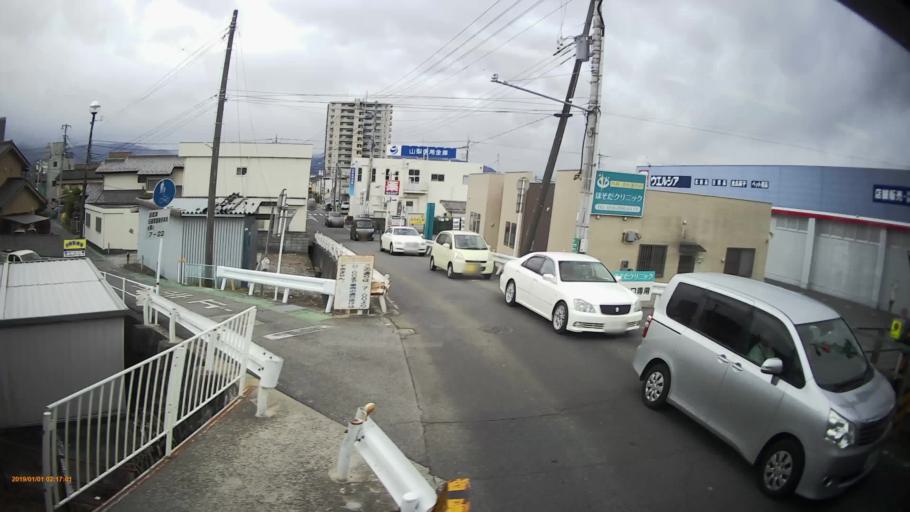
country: JP
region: Yamanashi
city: Kofu-shi
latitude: 35.6694
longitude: 138.5426
